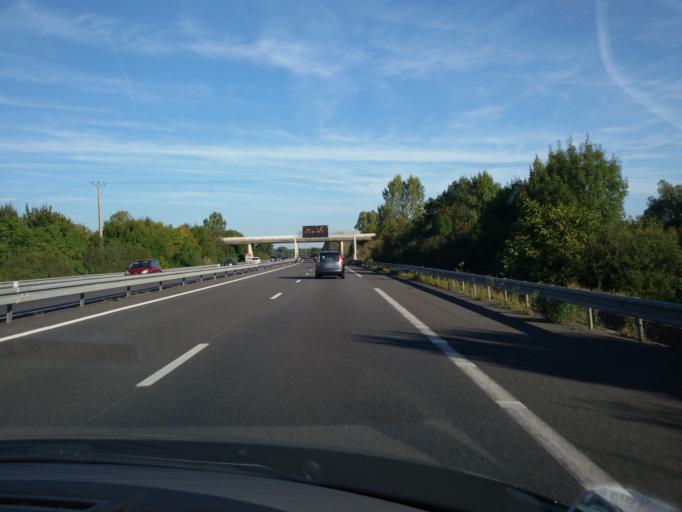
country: FR
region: Centre
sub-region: Departement du Cher
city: Foecy
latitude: 47.1854
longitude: 2.1695
